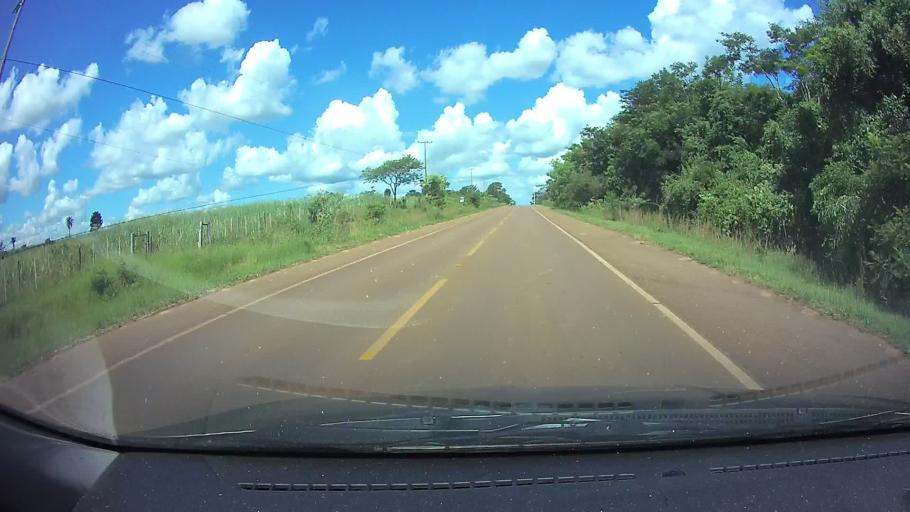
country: PY
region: Paraguari
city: La Colmena
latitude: -25.8994
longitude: -56.7858
